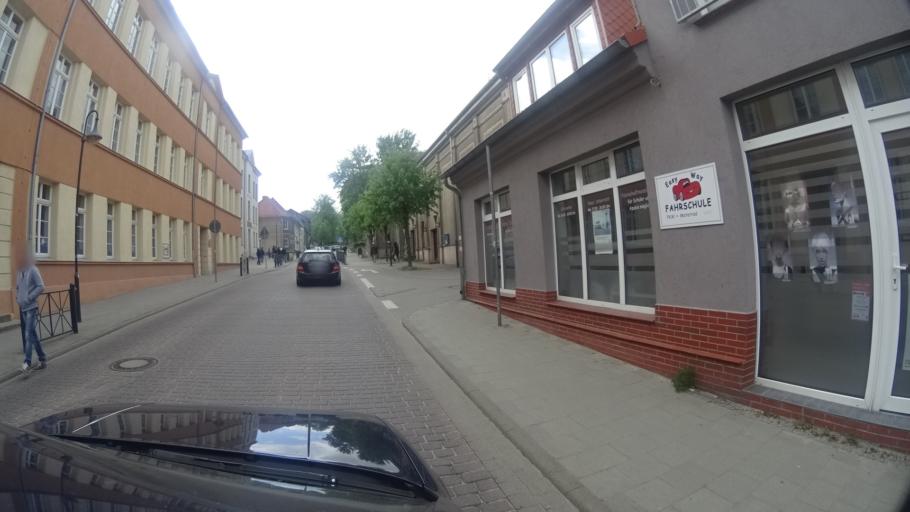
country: DE
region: Mecklenburg-Vorpommern
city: Malchow
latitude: 53.4747
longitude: 12.4248
